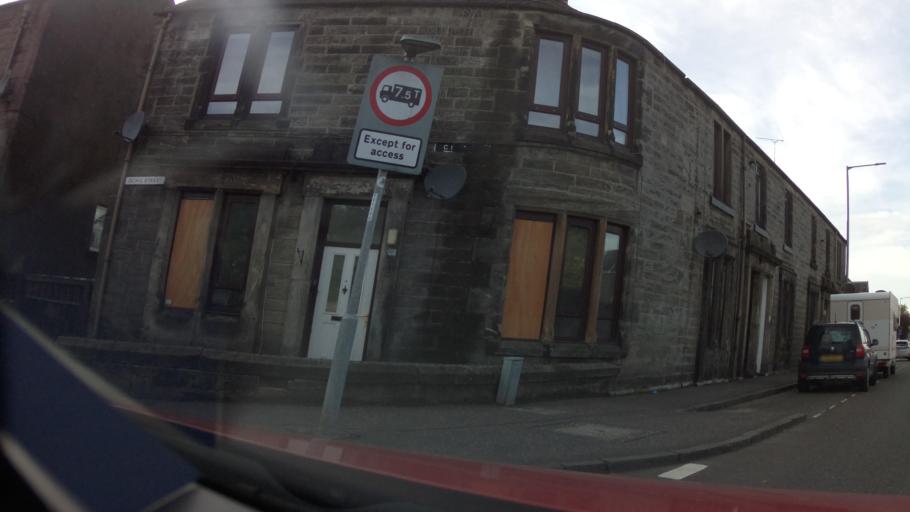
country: GB
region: Scotland
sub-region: Clackmannanshire
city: Alloa
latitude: 56.1194
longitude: -3.7978
